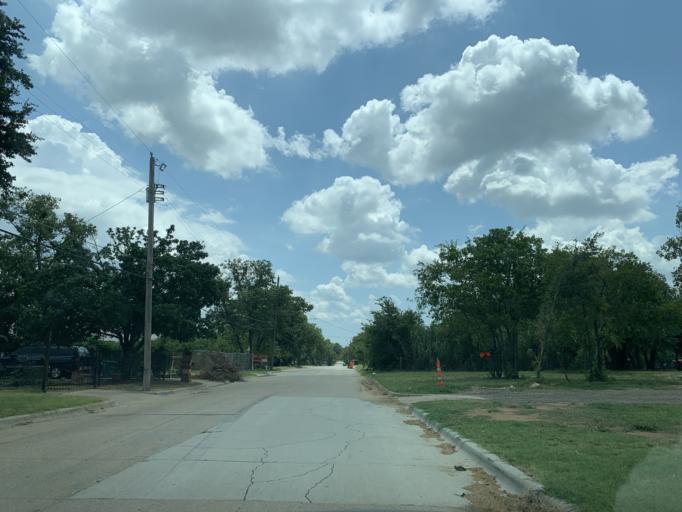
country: US
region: Texas
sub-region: Tarrant County
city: Forest Hill
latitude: 32.7300
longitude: -97.2574
